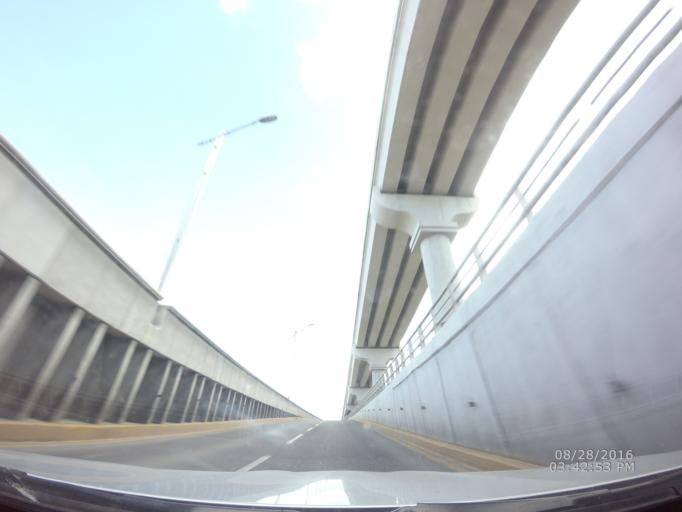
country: MX
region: Hidalgo
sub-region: Mineral de la Reforma
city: PRI Chacon
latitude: 20.0888
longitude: -98.7499
